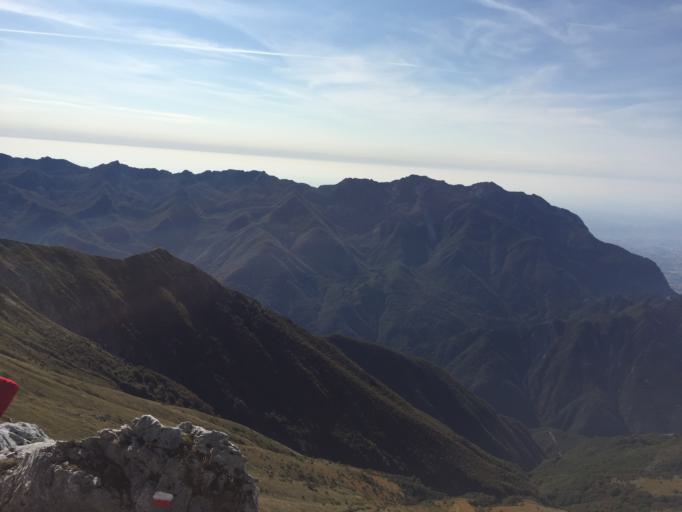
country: IT
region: Friuli Venezia Giulia
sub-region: Provincia di Udine
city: Resiutta
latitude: 46.3583
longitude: 13.1970
